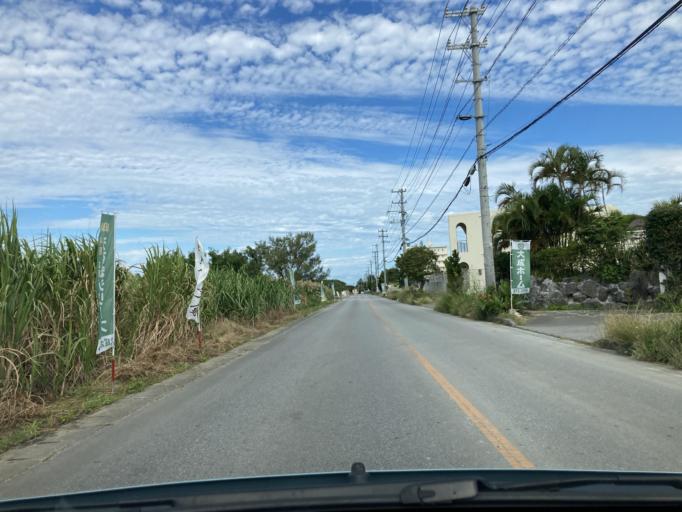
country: JP
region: Okinawa
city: Ishikawa
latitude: 26.4249
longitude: 127.7302
